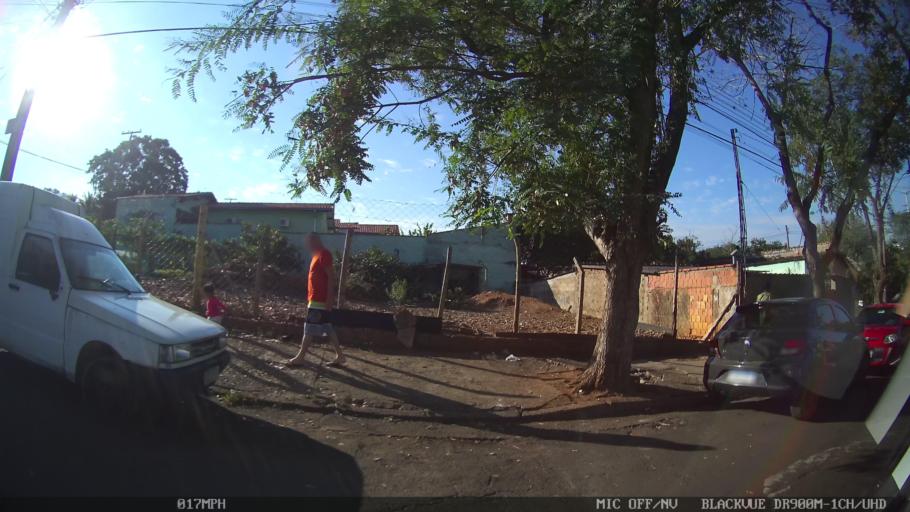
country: BR
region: Sao Paulo
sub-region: Piracicaba
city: Piracicaba
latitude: -22.6869
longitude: -47.6347
